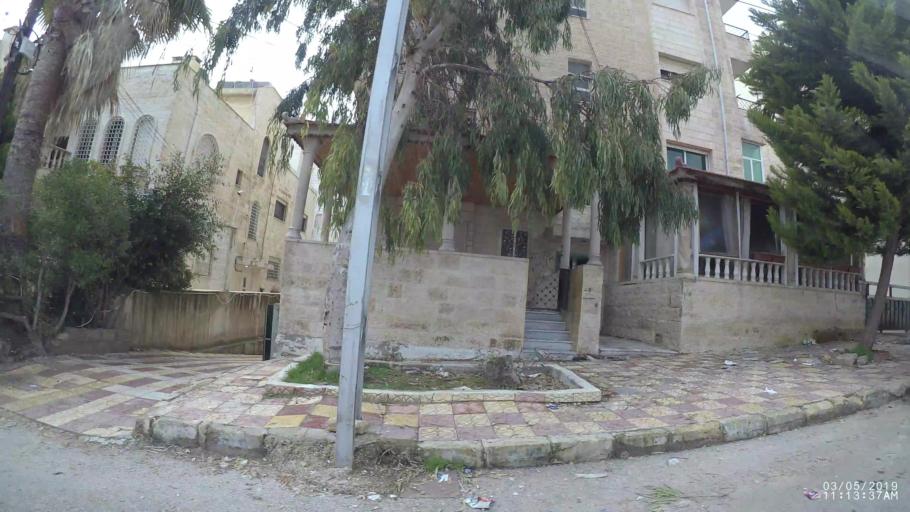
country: JO
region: Amman
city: Amman
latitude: 31.9908
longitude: 35.9275
